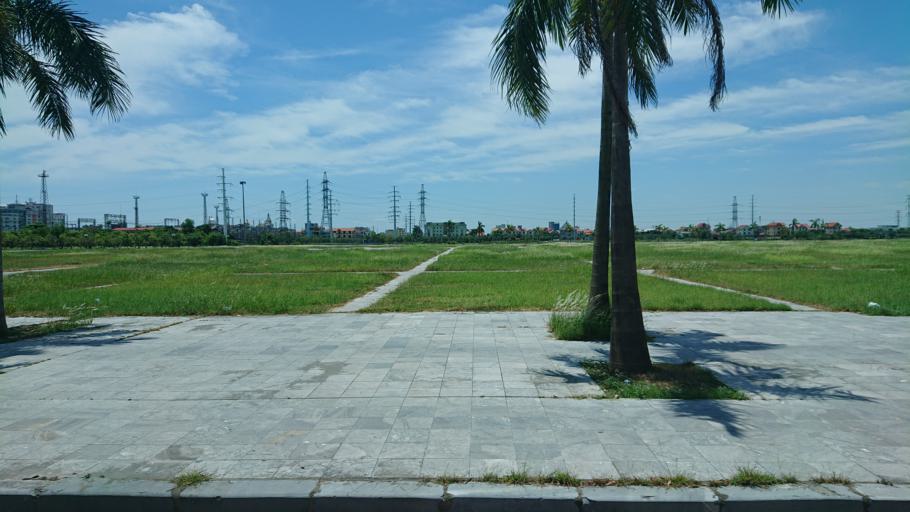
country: VN
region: Ninh Binh
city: Thanh Pho Ninh Binh
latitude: 20.2703
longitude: 105.9721
